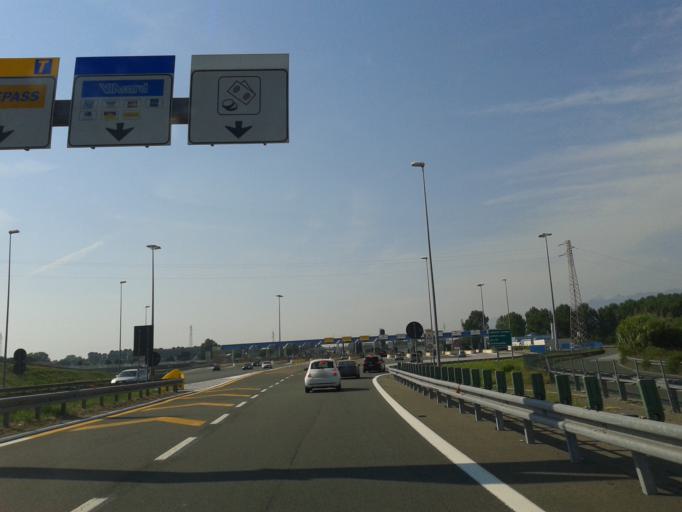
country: IT
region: Tuscany
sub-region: Provincia di Lucca
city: Viareggio
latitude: 43.8914
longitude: 10.2616
